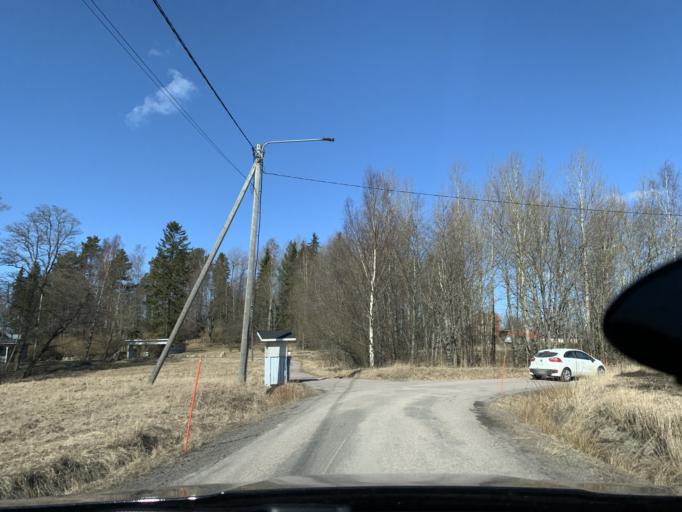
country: FI
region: Uusimaa
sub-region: Helsinki
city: Espoo
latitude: 60.1735
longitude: 24.5817
